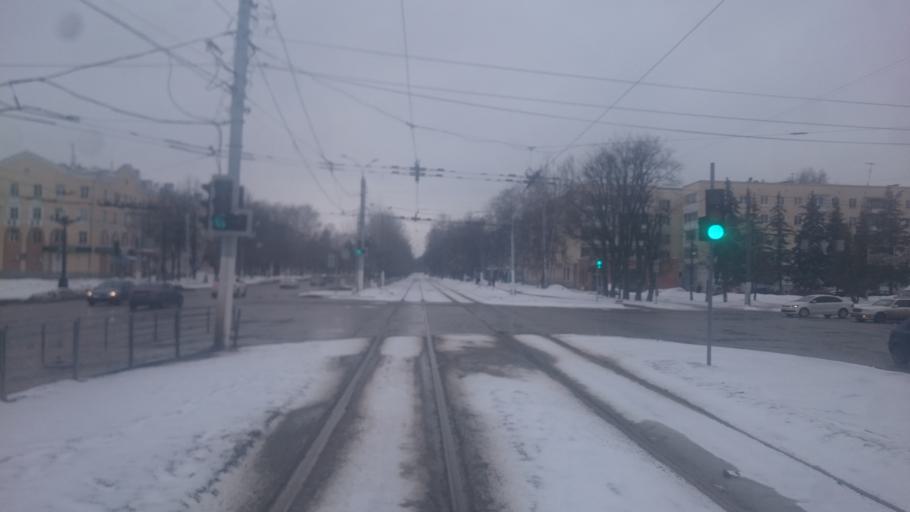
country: RU
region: Tverskaya
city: Tver
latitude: 56.8740
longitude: 35.8515
